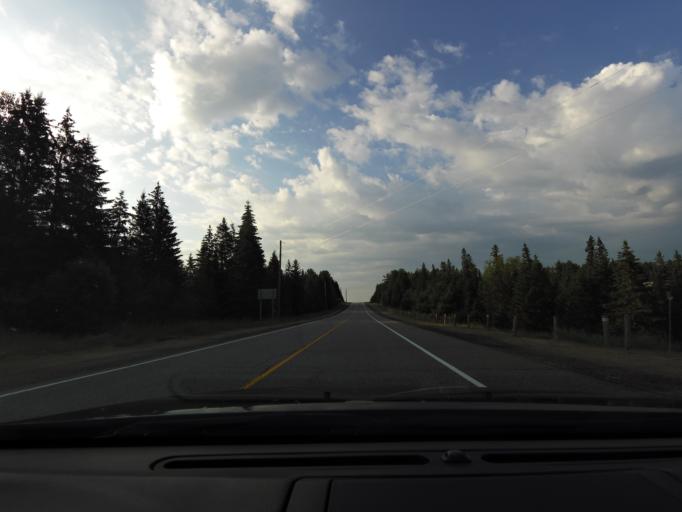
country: CA
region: Ontario
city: Huntsville
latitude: 45.5221
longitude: -79.3155
